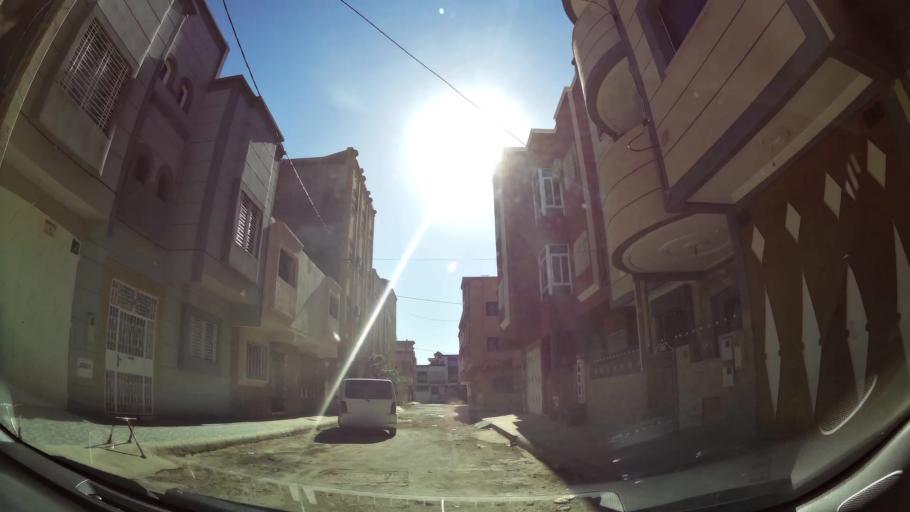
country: MA
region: Oriental
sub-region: Berkane-Taourirt
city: Berkane
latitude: 34.9378
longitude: -2.3328
